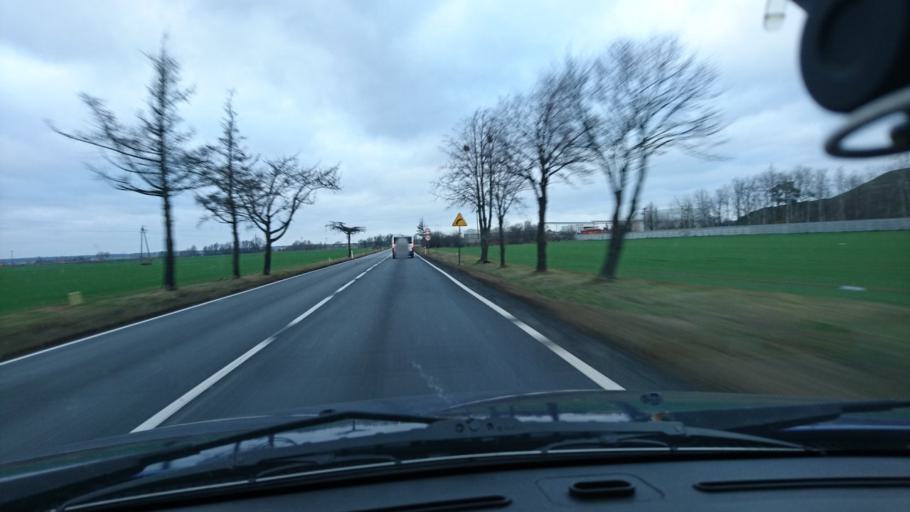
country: PL
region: Opole Voivodeship
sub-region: Powiat kluczborski
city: Kluczbork
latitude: 50.9996
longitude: 18.2065
